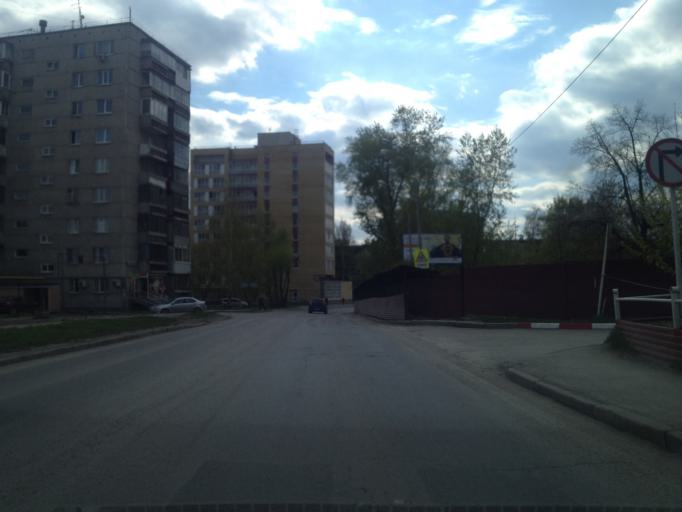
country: RU
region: Sverdlovsk
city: Yekaterinburg
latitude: 56.8568
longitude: 60.5897
